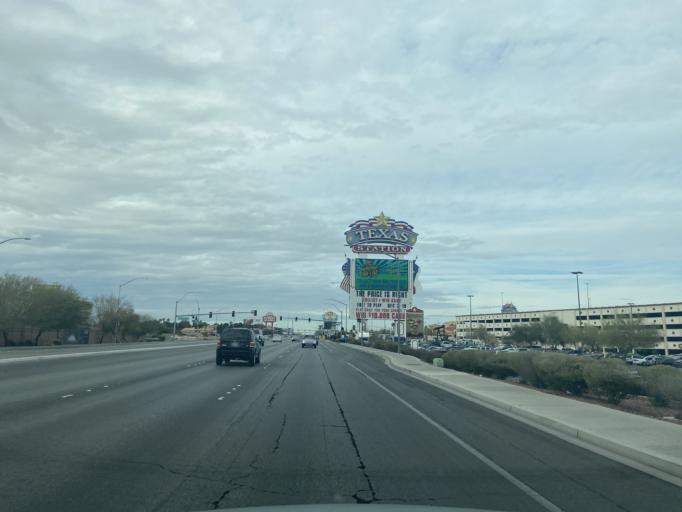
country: US
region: Nevada
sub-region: Clark County
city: Las Vegas
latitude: 36.1970
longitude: -115.1935
